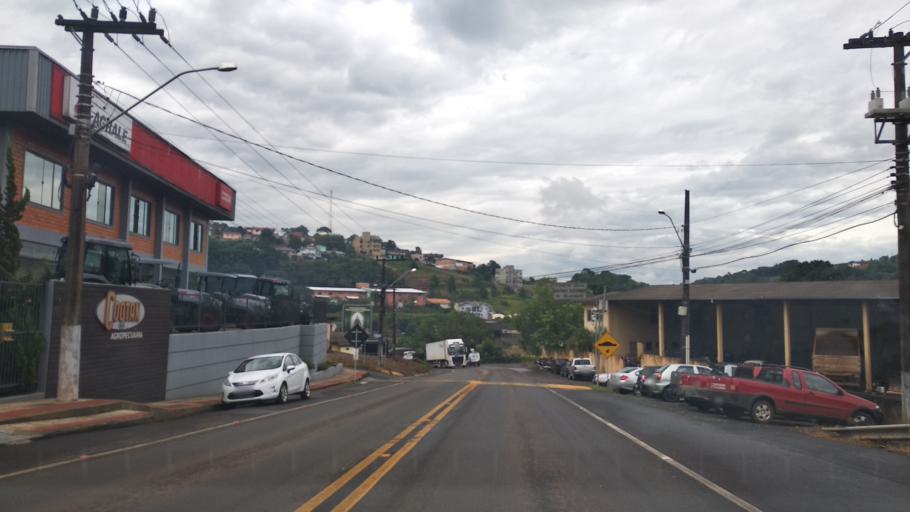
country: BR
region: Santa Catarina
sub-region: Videira
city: Videira
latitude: -27.0938
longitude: -51.2456
